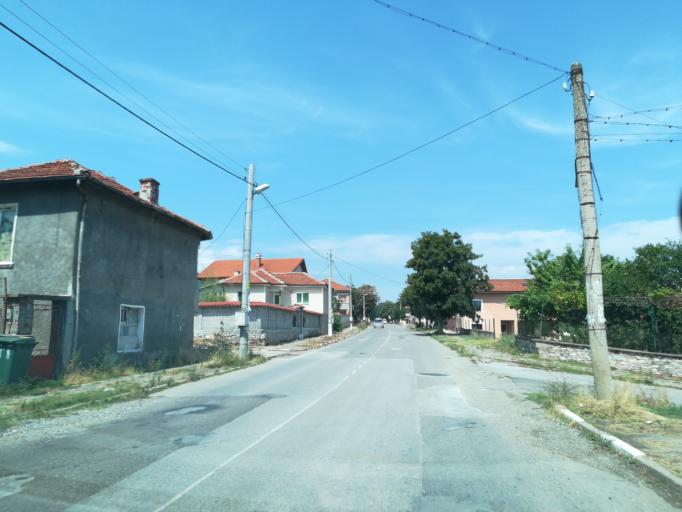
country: BG
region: Plovdiv
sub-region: Obshtina Asenovgrad
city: Asenovgrad
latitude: 41.9470
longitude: 24.9597
